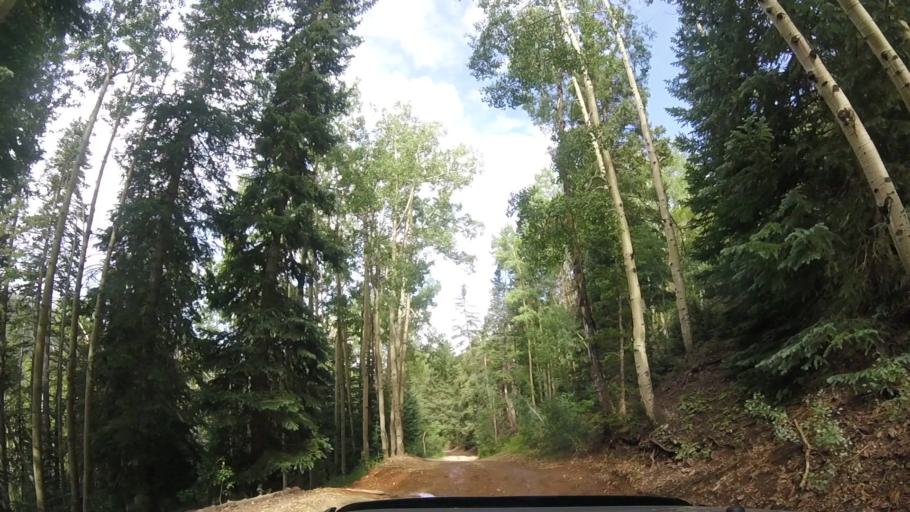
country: US
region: Colorado
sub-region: San Miguel County
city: Telluride
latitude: 37.8596
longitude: -107.7950
